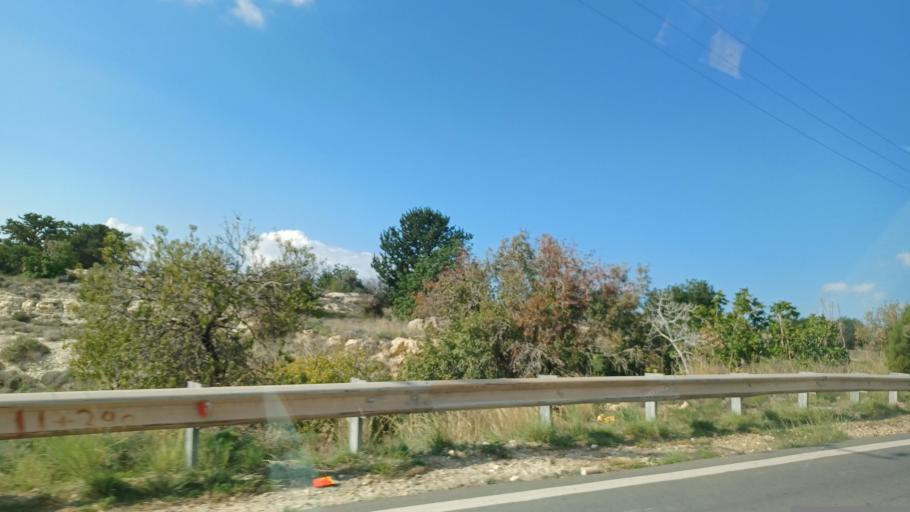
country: CY
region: Pafos
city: Paphos
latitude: 34.7709
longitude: 32.4584
